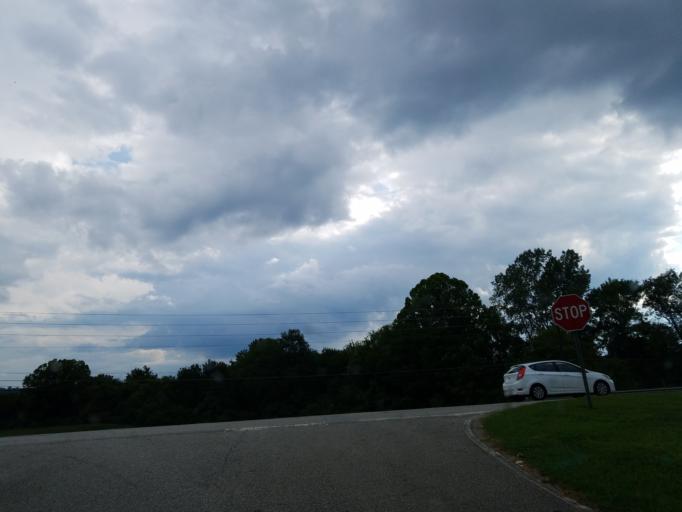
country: US
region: Georgia
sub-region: Floyd County
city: Shannon
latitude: 34.3890
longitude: -85.1819
